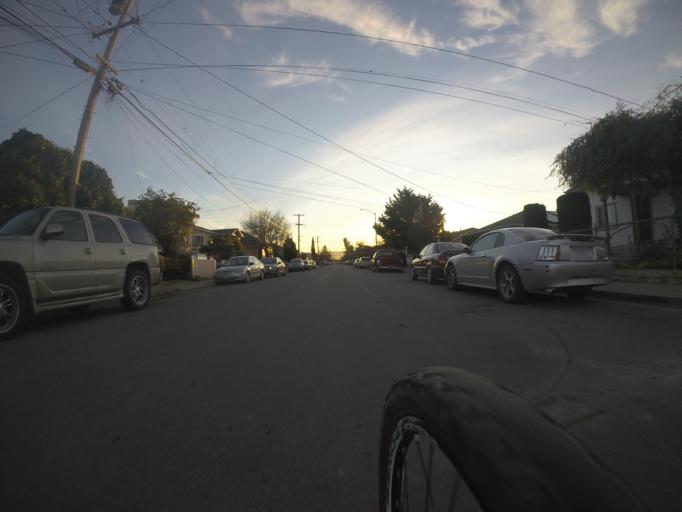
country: US
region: California
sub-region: Santa Clara County
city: Milpitas
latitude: 37.4312
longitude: -121.9675
